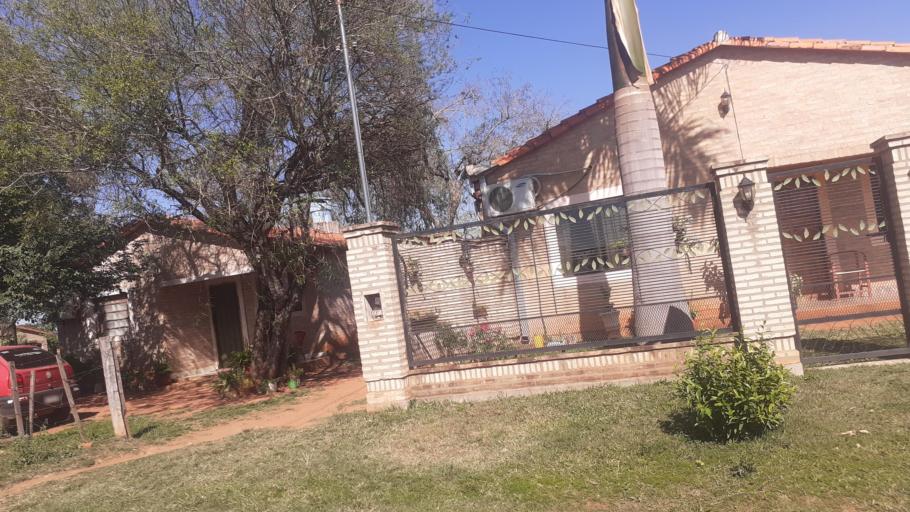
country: PY
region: Misiones
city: San Juan Bautista
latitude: -26.6661
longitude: -57.1271
